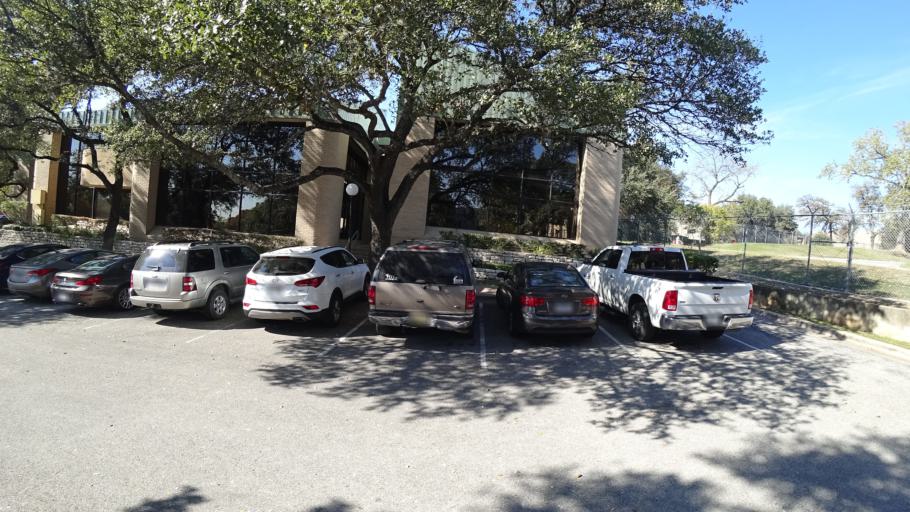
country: US
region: Texas
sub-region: Williamson County
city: Jollyville
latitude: 30.3715
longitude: -97.7556
